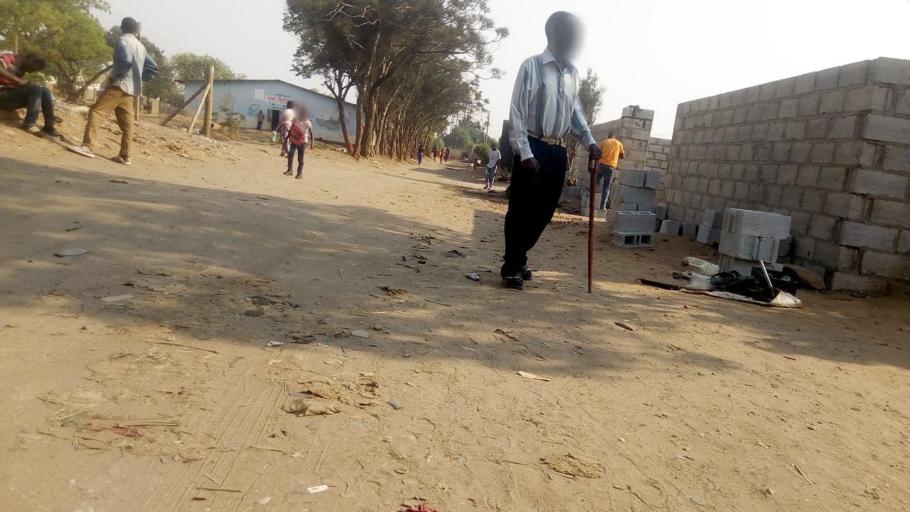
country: ZM
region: Lusaka
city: Lusaka
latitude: -15.3624
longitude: 28.2918
